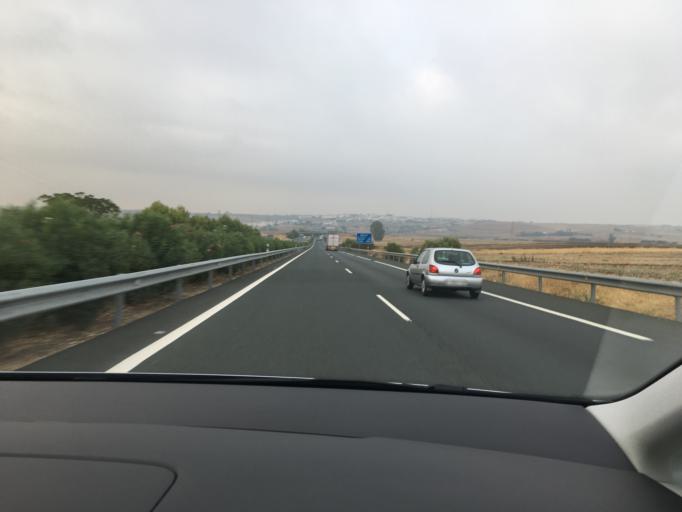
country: ES
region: Andalusia
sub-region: Province of Cordoba
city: La Carlota
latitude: 37.6921
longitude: -4.9212
